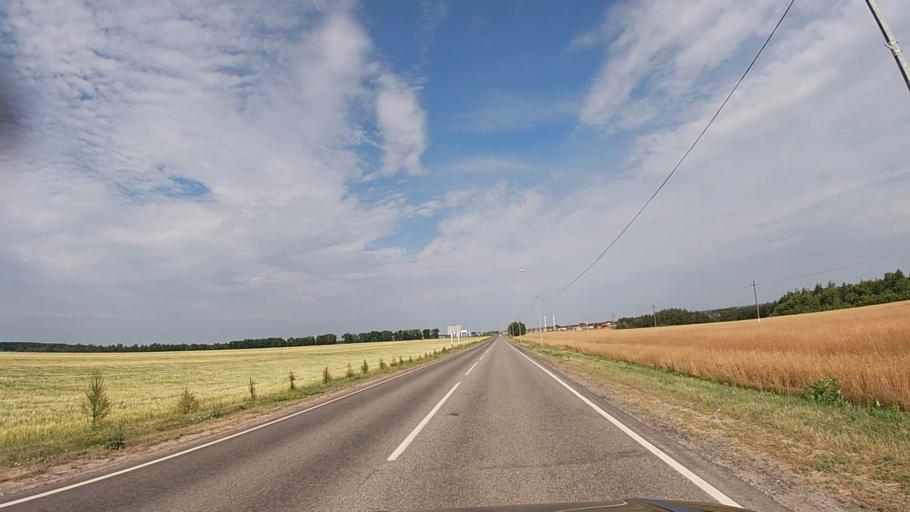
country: RU
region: Belgorod
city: Krasnaya Yaruga
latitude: 50.7962
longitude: 35.7064
